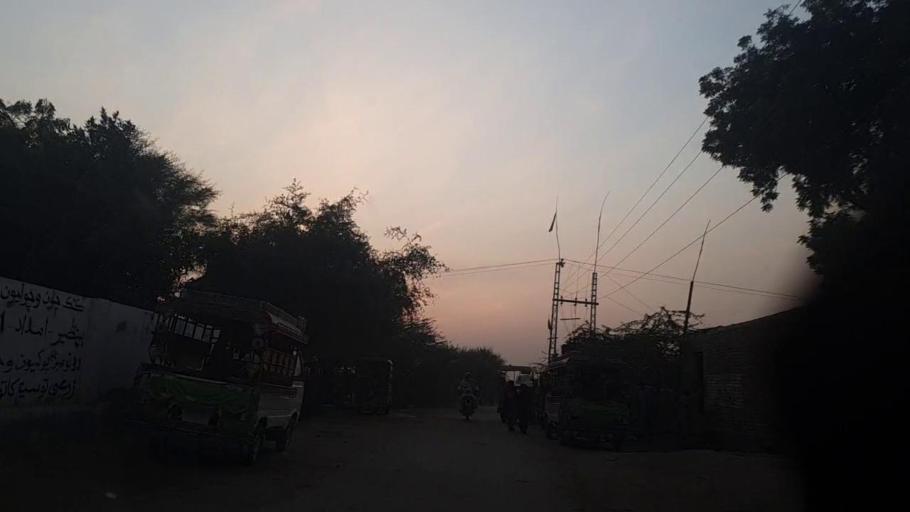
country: PK
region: Sindh
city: Sakrand
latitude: 26.1023
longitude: 68.3101
